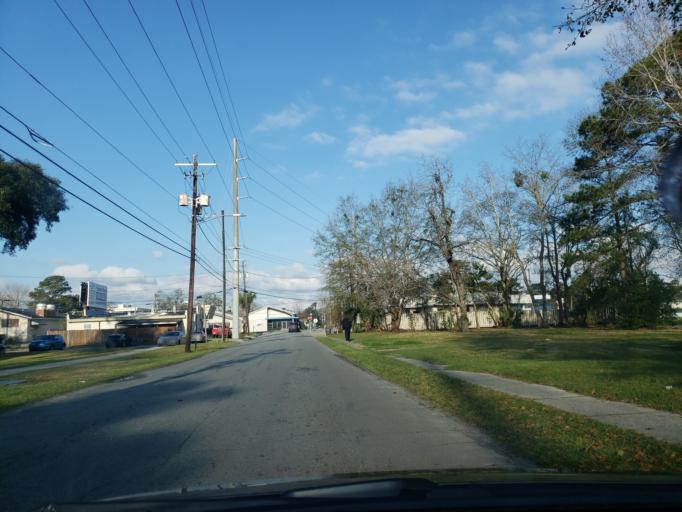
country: US
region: Georgia
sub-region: Chatham County
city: Thunderbolt
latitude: 32.0286
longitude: -81.0919
